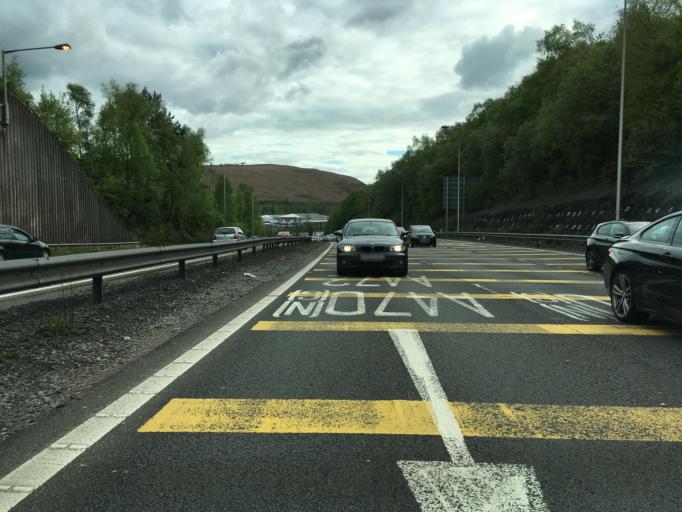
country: GB
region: Wales
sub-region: Merthyr Tydfil County Borough
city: Treharris
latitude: 51.6510
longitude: -3.3167
